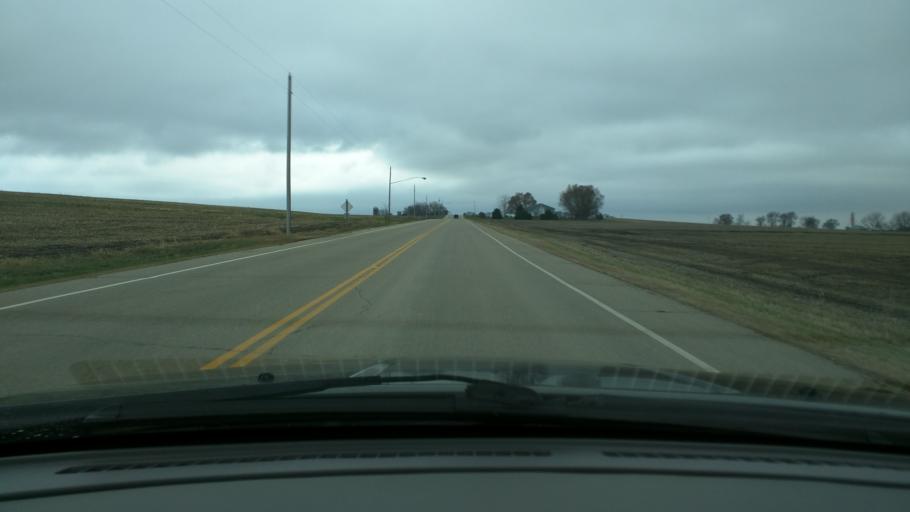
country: US
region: Minnesota
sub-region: Washington County
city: Cottage Grove
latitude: 44.7623
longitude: -92.9239
